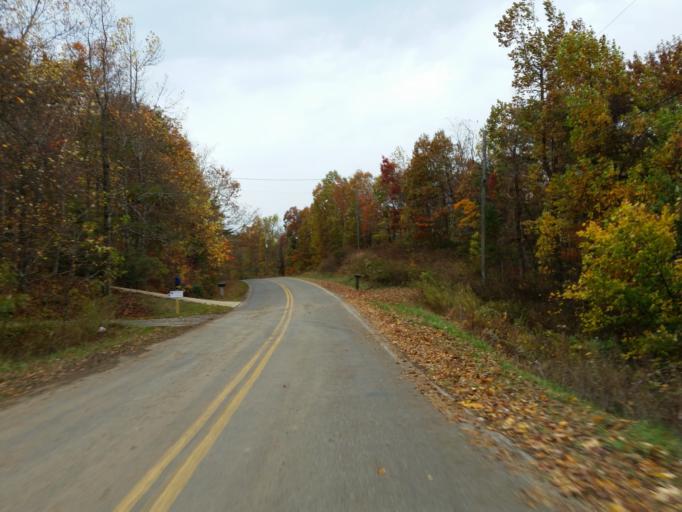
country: US
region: Georgia
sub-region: Pickens County
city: Jasper
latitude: 34.5586
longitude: -84.3464
